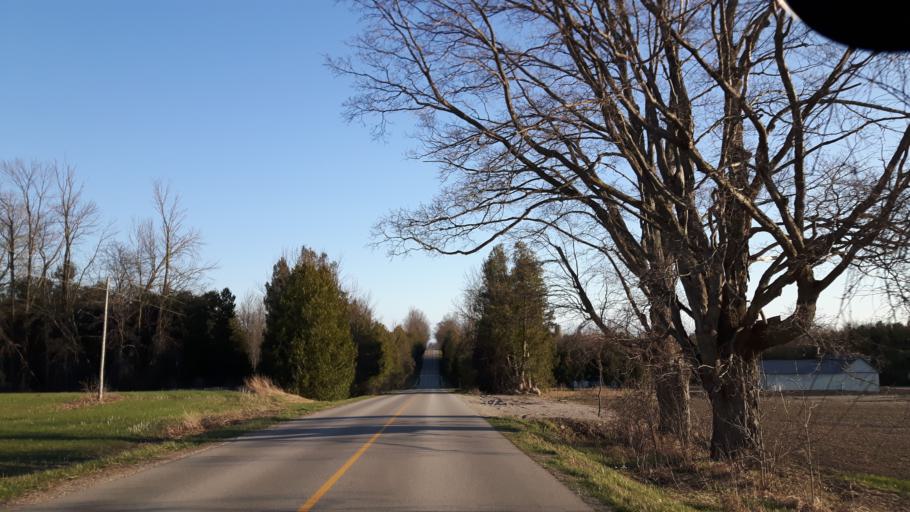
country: CA
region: Ontario
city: Goderich
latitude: 43.6595
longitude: -81.6846
